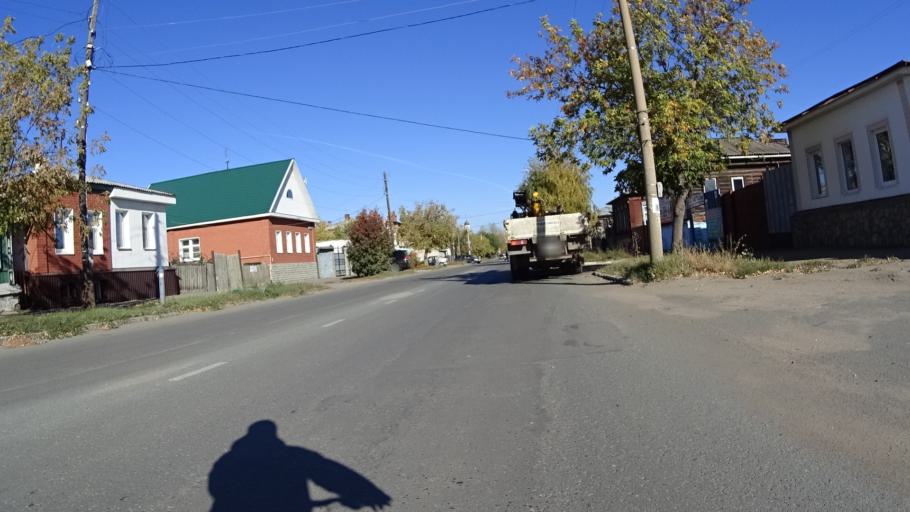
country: RU
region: Chelyabinsk
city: Troitsk
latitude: 54.0850
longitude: 61.5655
